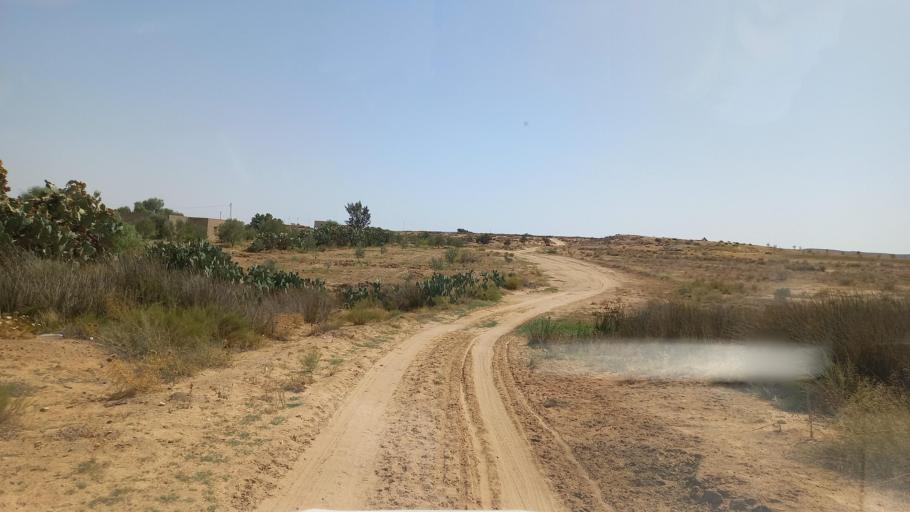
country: TN
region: Al Qasrayn
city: Kasserine
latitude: 35.2230
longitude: 9.0360
